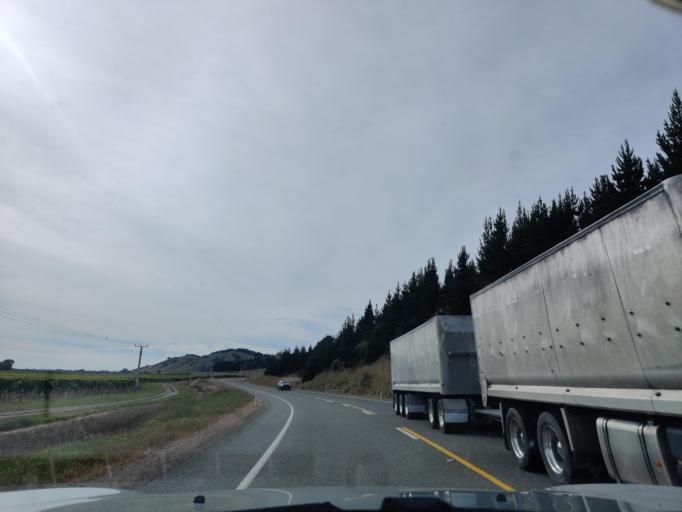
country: NZ
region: Marlborough
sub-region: Marlborough District
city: Blenheim
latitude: -41.5340
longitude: 173.6611
